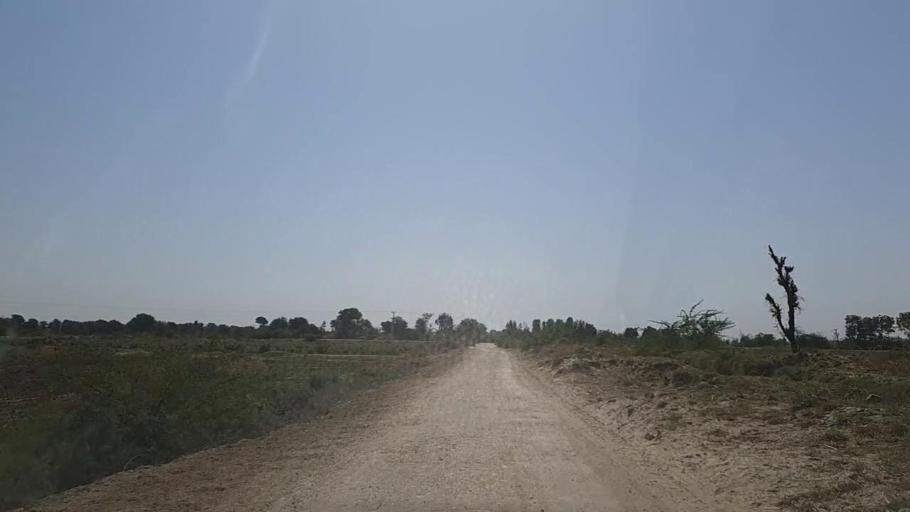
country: PK
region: Sindh
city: Samaro
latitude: 25.2454
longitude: 69.4111
